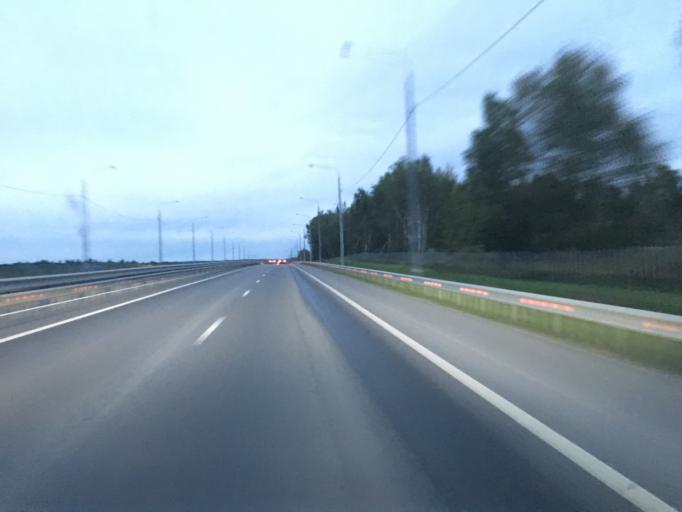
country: RU
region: Kaluga
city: Maloyaroslavets
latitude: 54.9433
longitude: 36.4345
